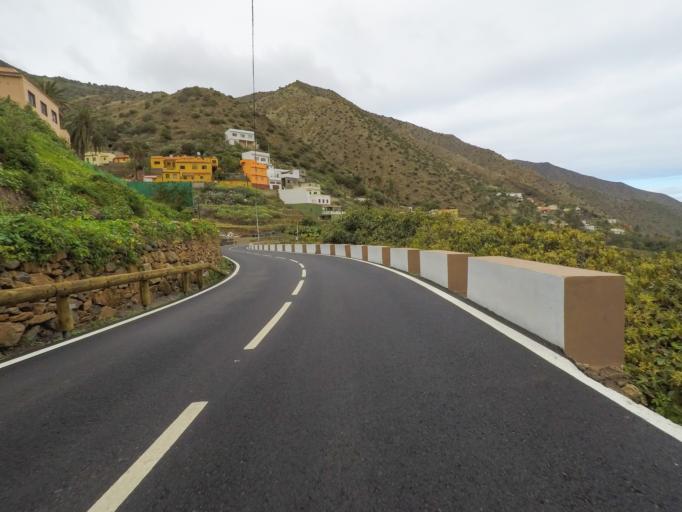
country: ES
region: Canary Islands
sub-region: Provincia de Santa Cruz de Tenerife
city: Vallehermosa
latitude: 28.1838
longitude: -17.2644
